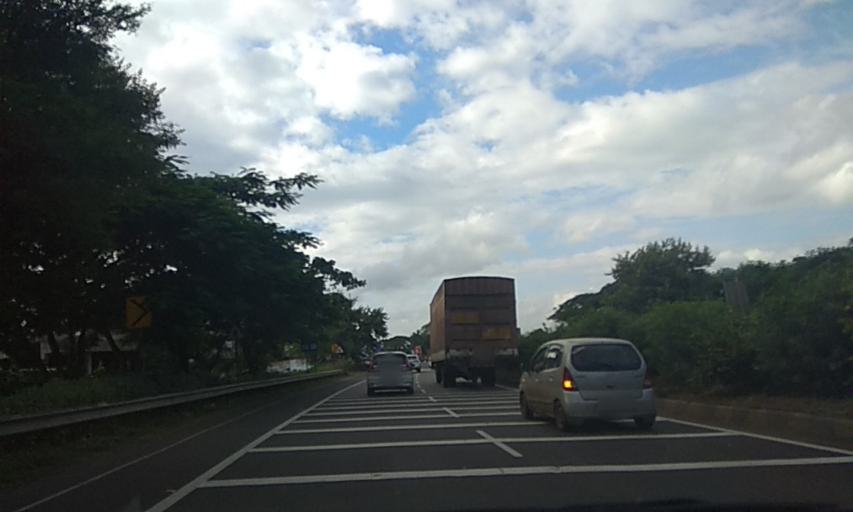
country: IN
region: Maharashtra
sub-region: Satara Division
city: Karad
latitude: 17.1241
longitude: 74.1920
